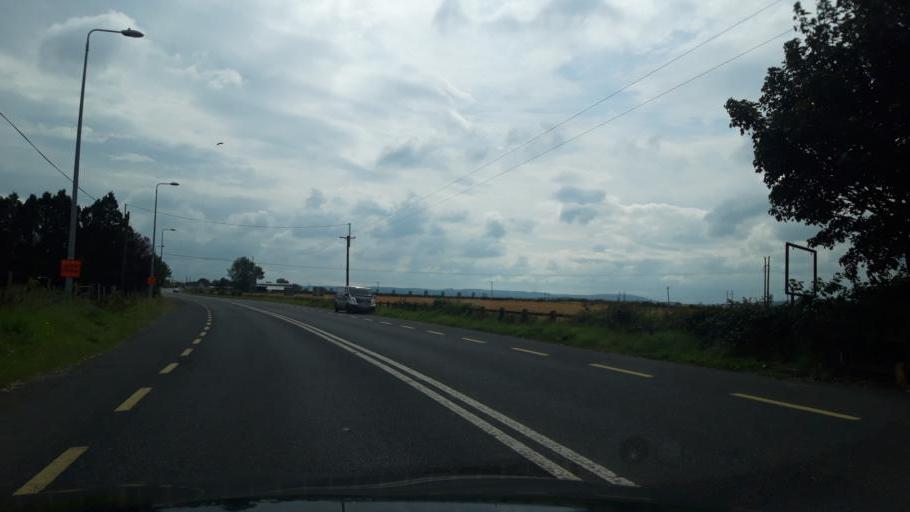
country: IE
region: Leinster
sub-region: Kildare
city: Athy
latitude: 52.9845
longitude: -7.0014
